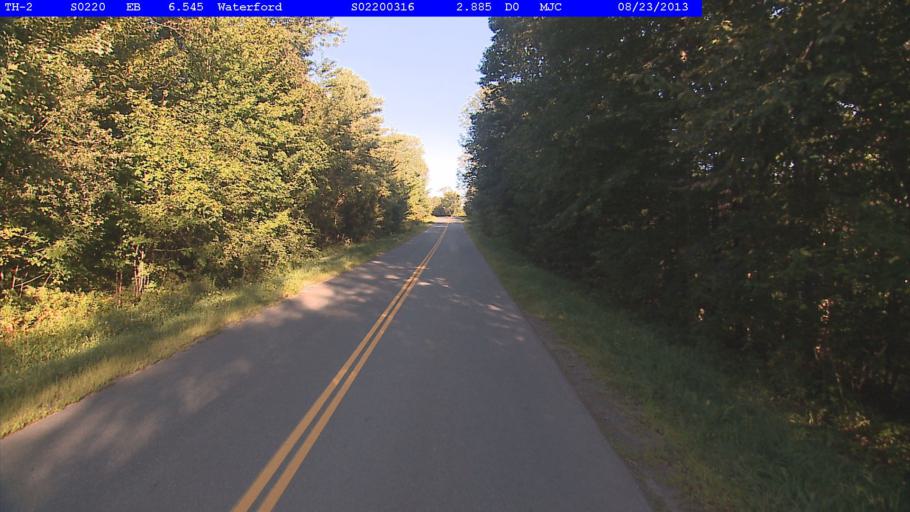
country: US
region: Vermont
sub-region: Caledonia County
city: Saint Johnsbury
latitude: 44.3400
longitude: -71.9459
